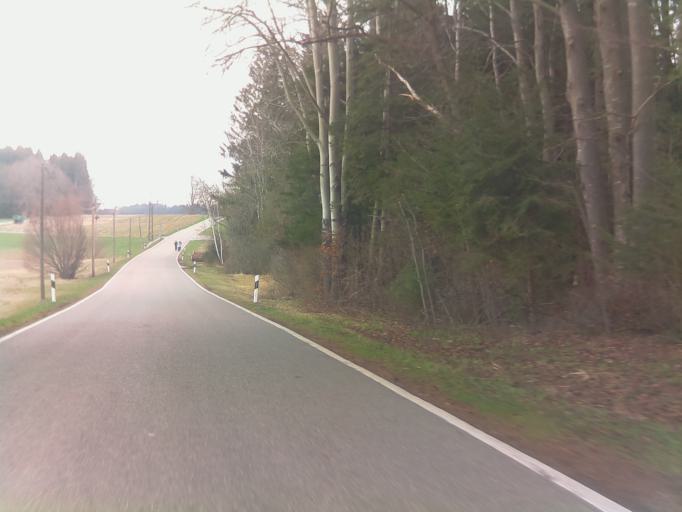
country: DE
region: Bavaria
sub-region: Upper Bavaria
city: Obersochering
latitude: 47.7477
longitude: 11.2216
